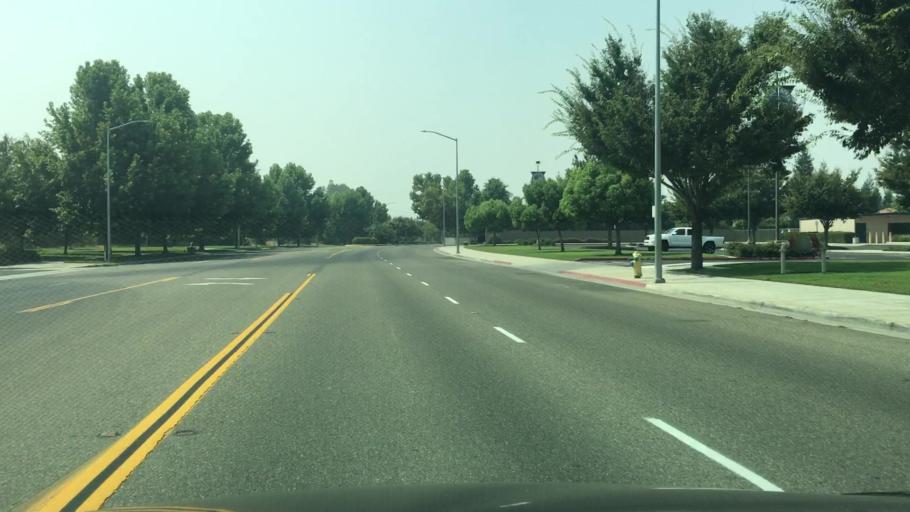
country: US
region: California
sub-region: Fresno County
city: Clovis
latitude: 36.8604
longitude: -119.7022
